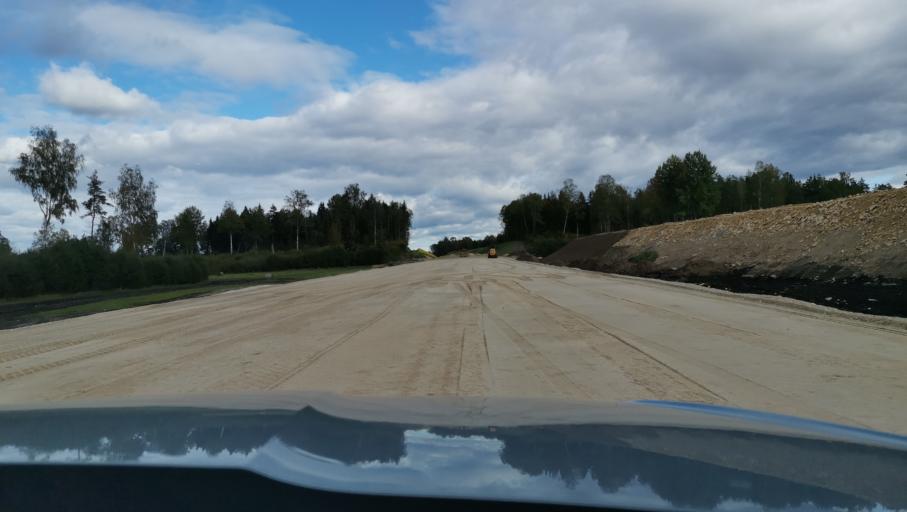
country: EE
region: Harju
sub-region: Keila linn
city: Keila
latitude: 59.1461
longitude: 24.4981
